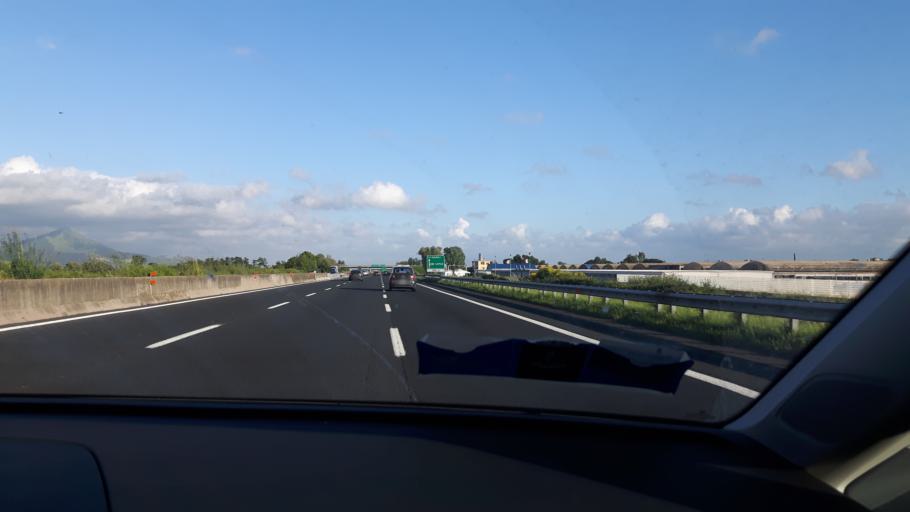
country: IT
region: Campania
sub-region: Provincia di Caserta
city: Pignataro Maggiore
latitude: 41.1700
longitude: 14.1728
